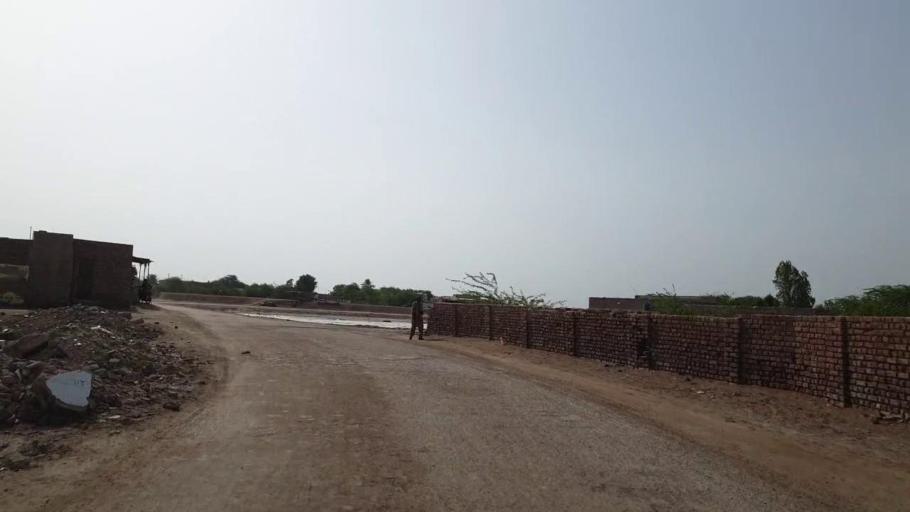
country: PK
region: Sindh
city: Jam Sahib
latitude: 26.2976
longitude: 68.6348
